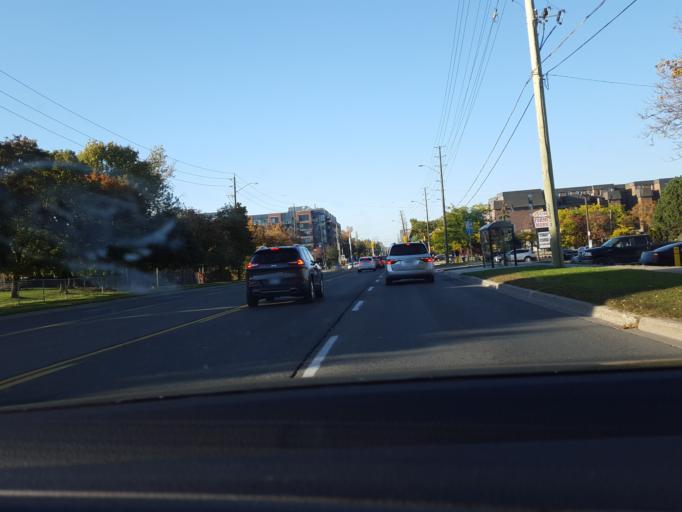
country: CA
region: Ontario
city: North York
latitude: 43.8101
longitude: -79.4230
